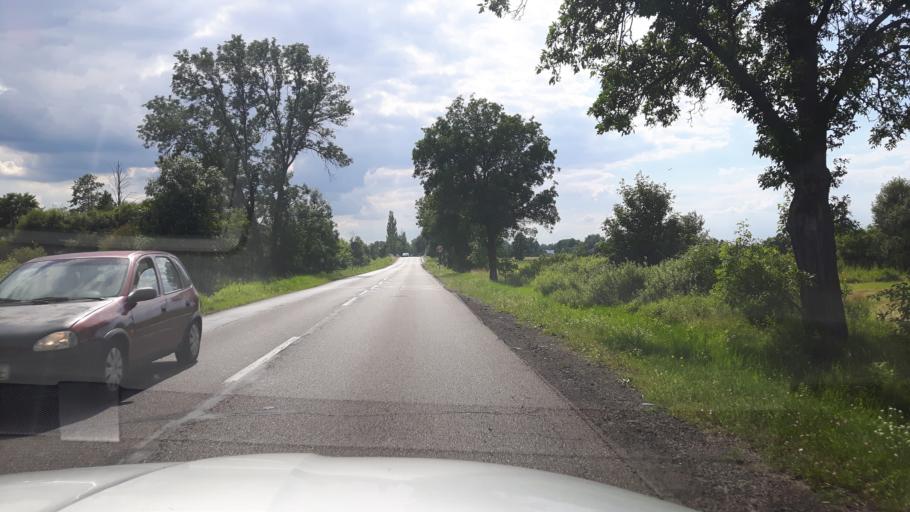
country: PL
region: Masovian Voivodeship
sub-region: Powiat wolominski
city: Ostrowek
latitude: 52.3776
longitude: 21.3549
